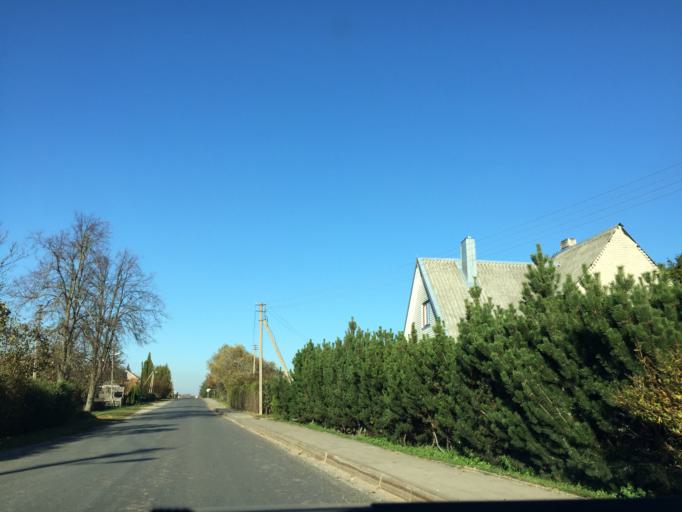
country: LT
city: Plateliai
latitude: 56.0447
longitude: 21.8173
